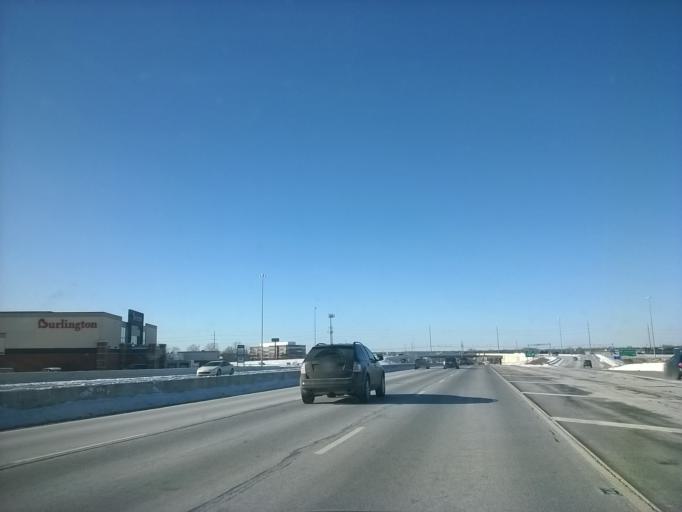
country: US
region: Indiana
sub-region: Hamilton County
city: Fishers
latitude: 39.9069
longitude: -86.0727
